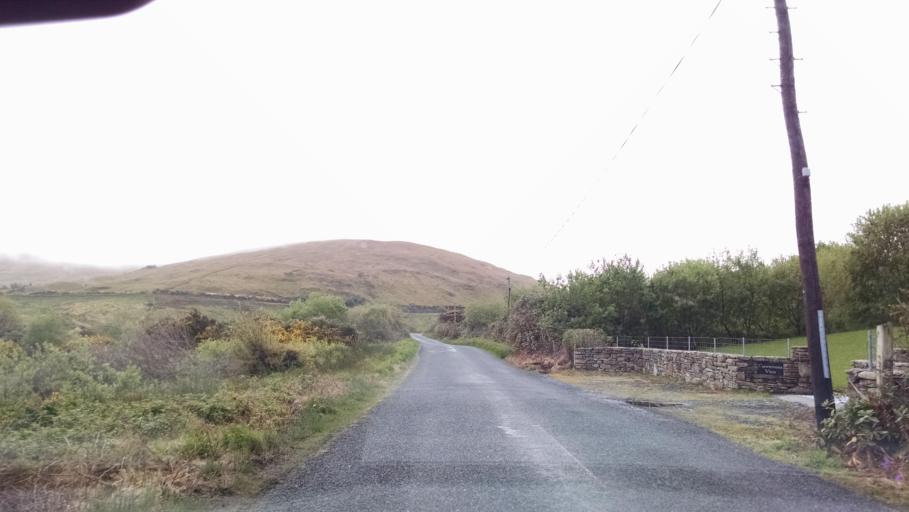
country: IE
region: Connaught
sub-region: Maigh Eo
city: Westport
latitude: 53.6130
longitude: -9.6790
